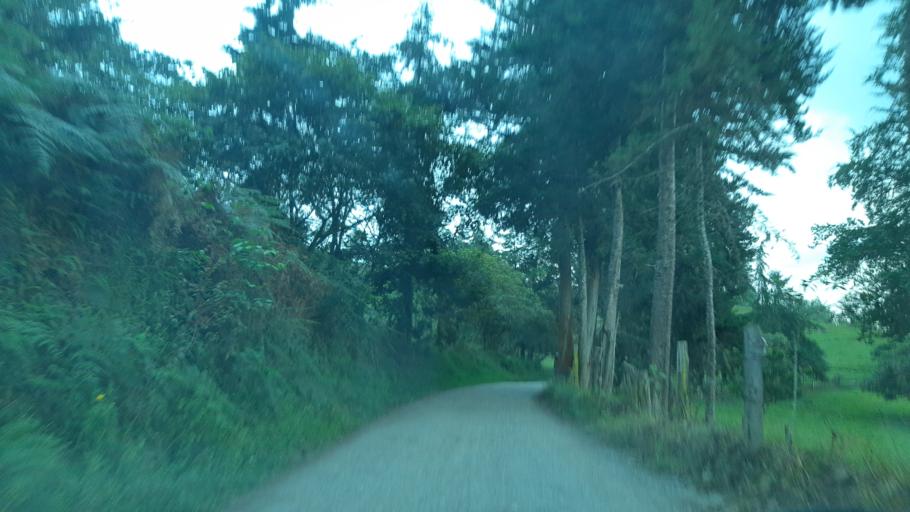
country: CO
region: Boyaca
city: Garagoa
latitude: 5.1031
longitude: -73.3612
